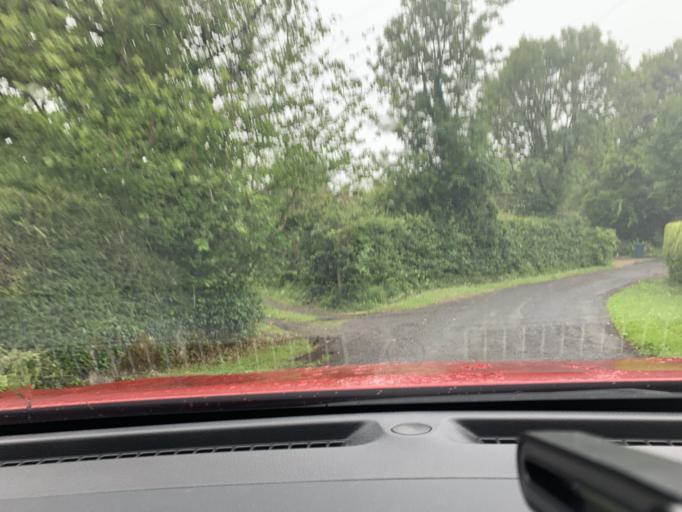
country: GB
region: Northern Ireland
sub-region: Fermanagh District
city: Enniskillen
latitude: 54.2635
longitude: -7.7389
